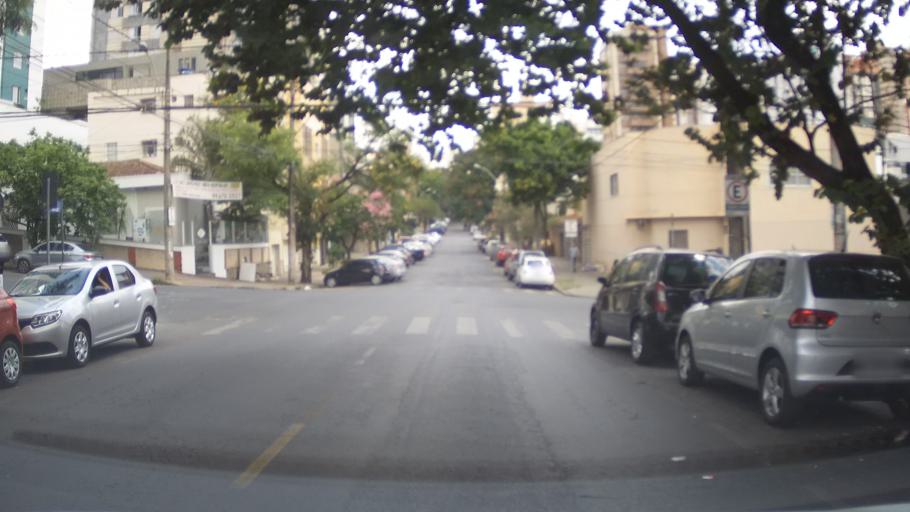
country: BR
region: Minas Gerais
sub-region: Belo Horizonte
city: Belo Horizonte
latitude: -19.9268
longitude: -43.9215
